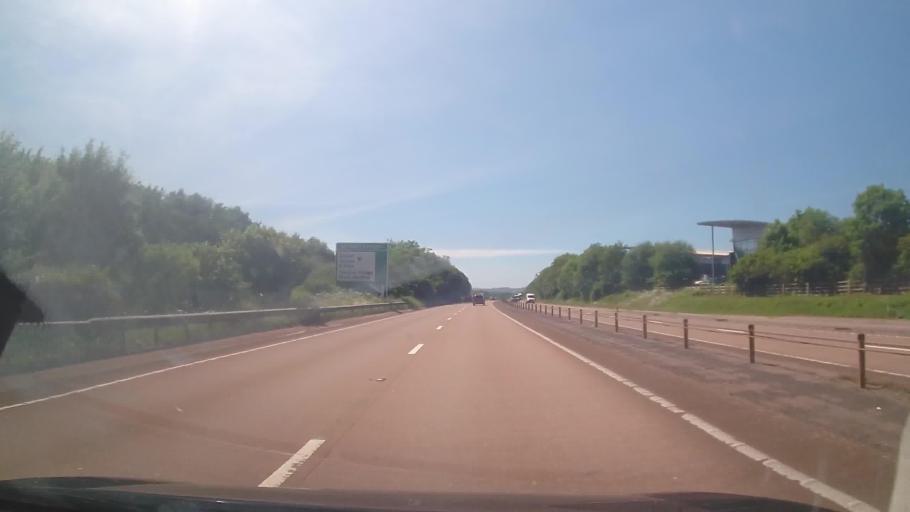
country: GB
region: England
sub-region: Devon
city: Topsham
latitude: 50.7286
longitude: -3.4125
